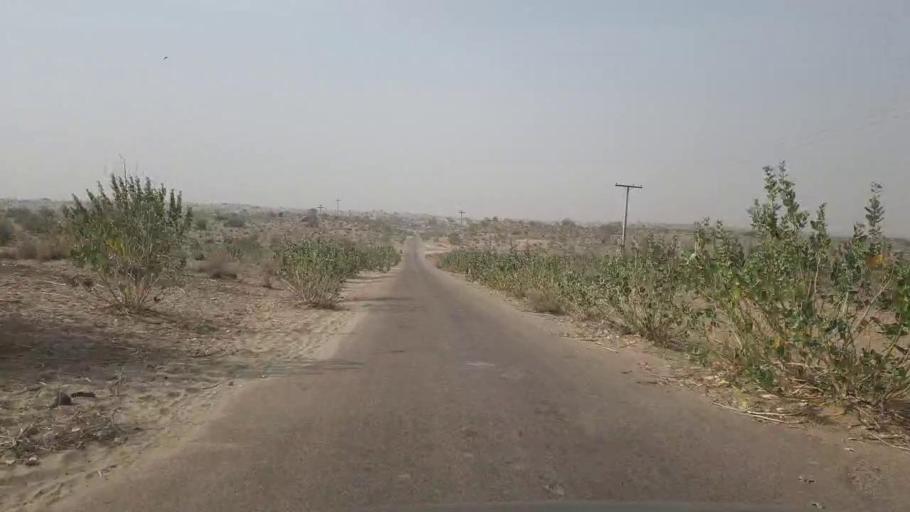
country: PK
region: Sindh
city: Chor
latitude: 25.6147
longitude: 69.9306
